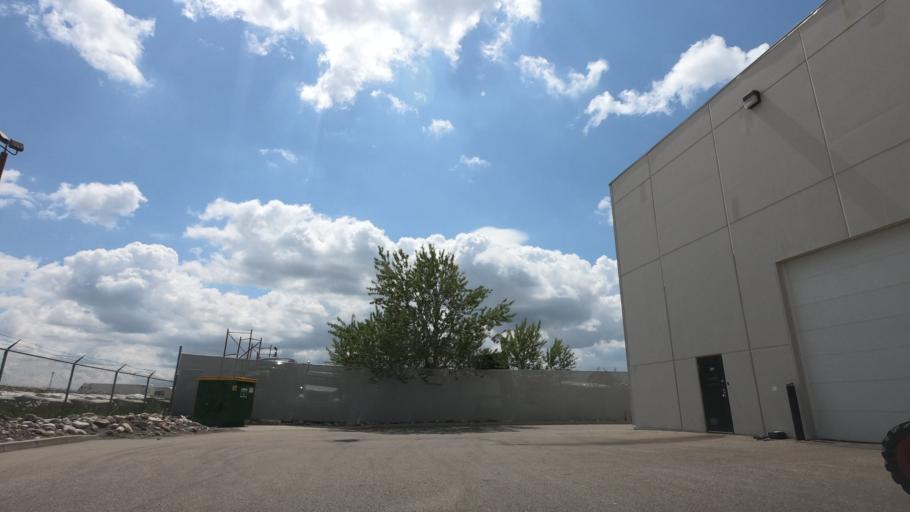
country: CA
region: Alberta
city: Airdrie
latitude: 51.2961
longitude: -113.9870
